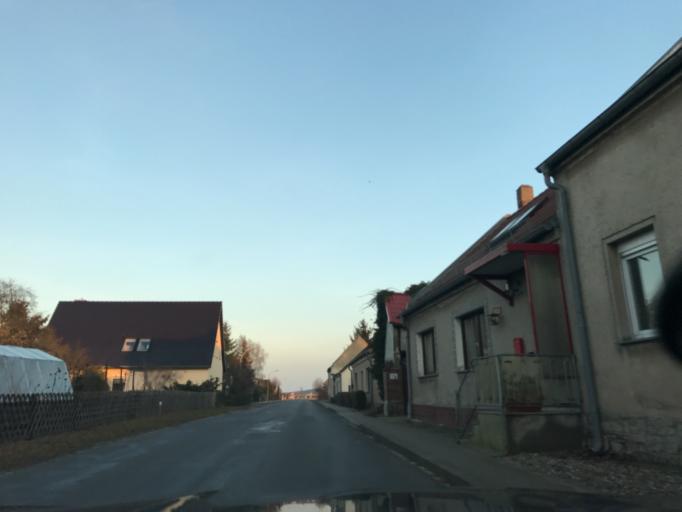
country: DE
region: Brandenburg
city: Wusterwitz
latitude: 52.4748
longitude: 12.4562
